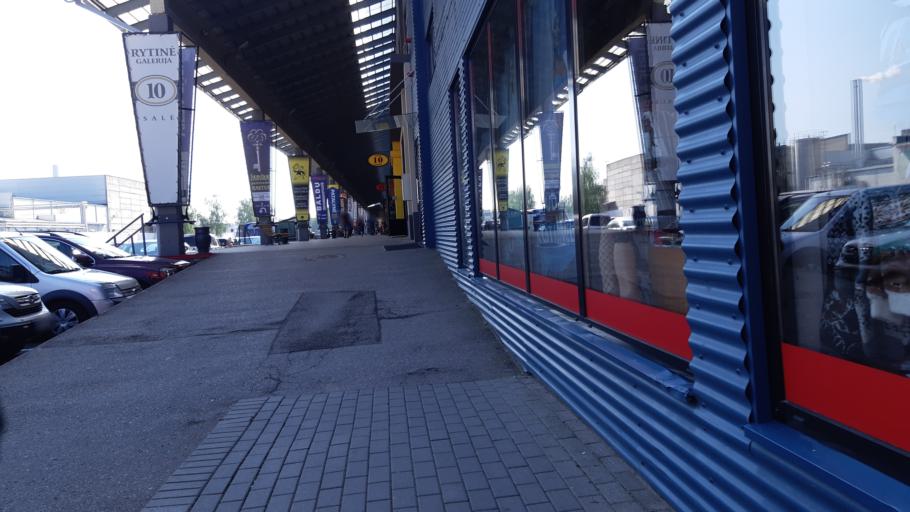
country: LT
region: Kauno apskritis
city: Dainava (Kaunas)
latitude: 54.9163
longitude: 23.9923
